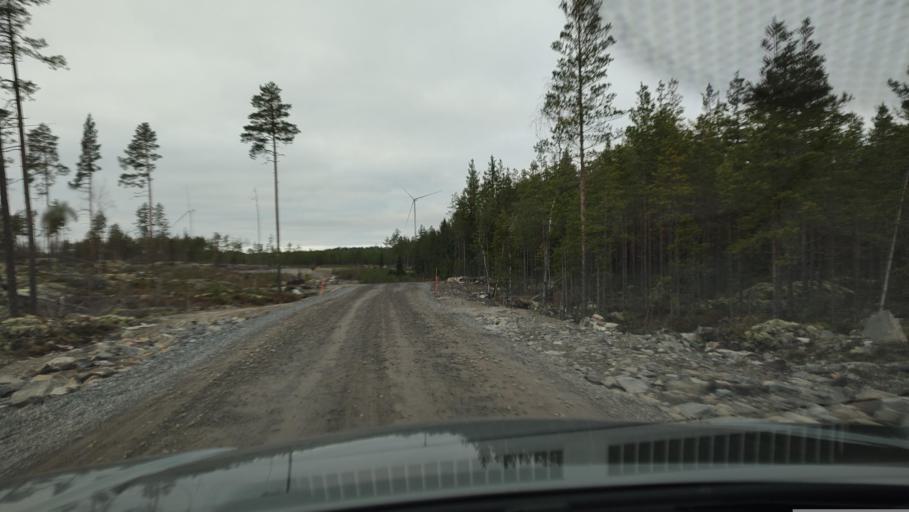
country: FI
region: Southern Ostrobothnia
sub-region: Suupohja
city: Karijoki
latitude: 62.1900
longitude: 21.5797
